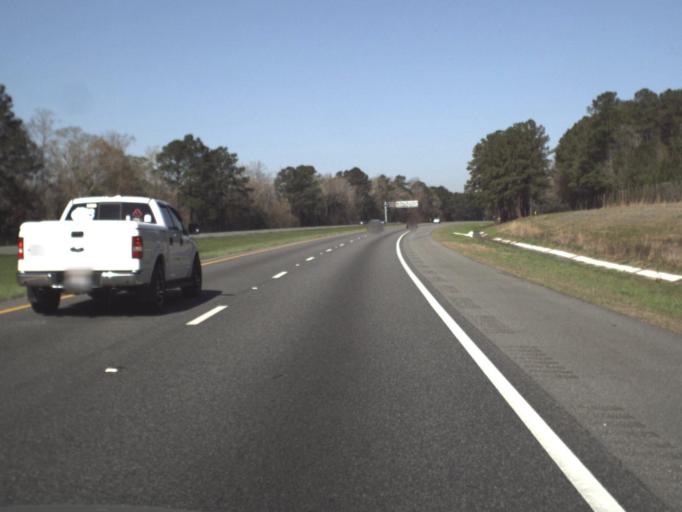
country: US
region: Florida
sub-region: Gadsden County
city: Midway
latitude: 30.4950
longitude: -84.4445
